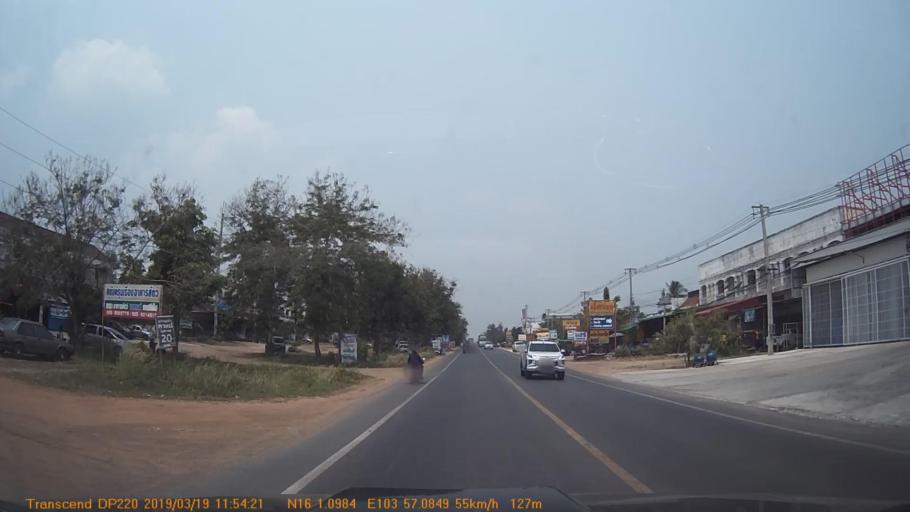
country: TH
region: Roi Et
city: Ban Selaphum
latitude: 16.0184
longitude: 103.9513
